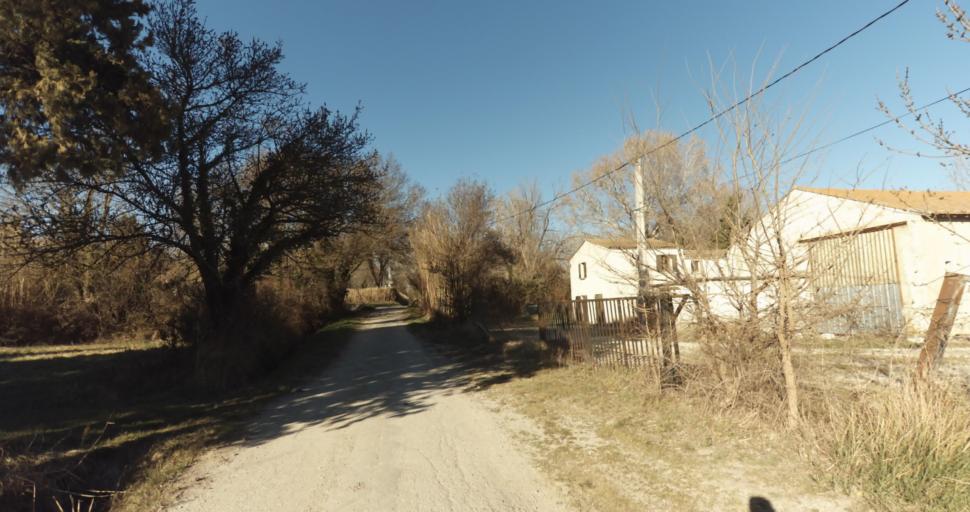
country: FR
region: Provence-Alpes-Cote d'Azur
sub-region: Departement des Bouches-du-Rhone
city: Barbentane
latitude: 43.9145
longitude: 4.7759
